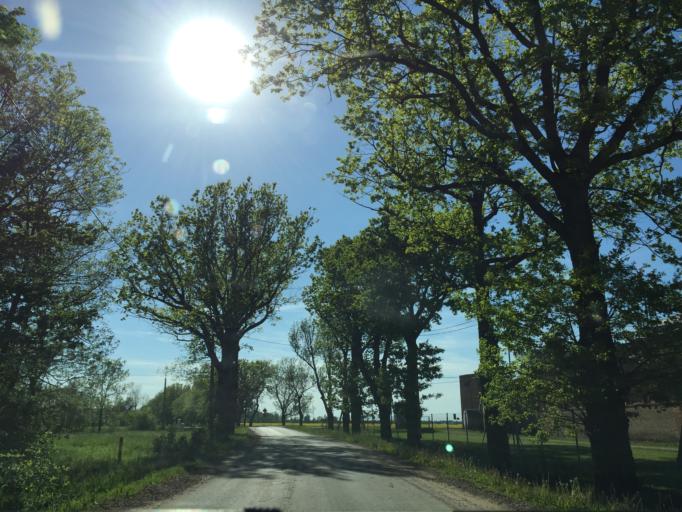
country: LV
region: Jelgava
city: Jelgava
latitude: 56.5203
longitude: 23.7509
